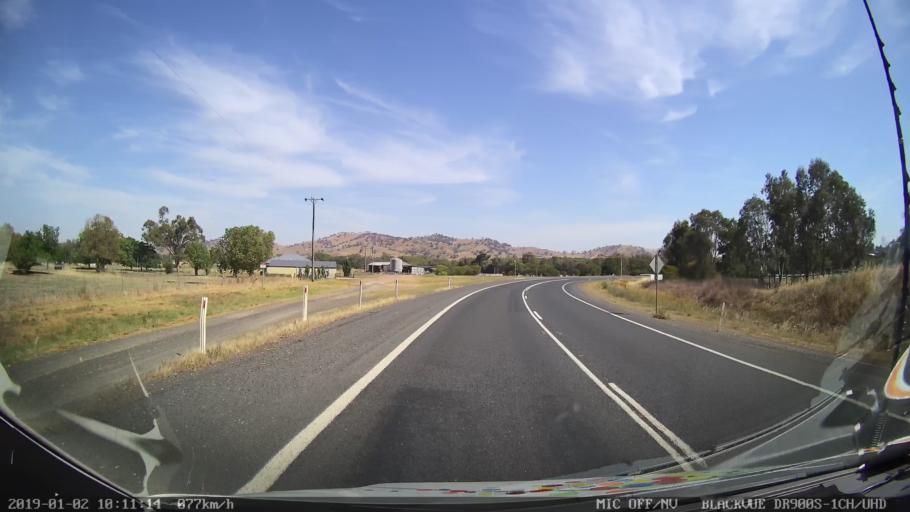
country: AU
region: New South Wales
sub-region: Gundagai
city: Gundagai
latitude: -35.0950
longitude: 148.0921
